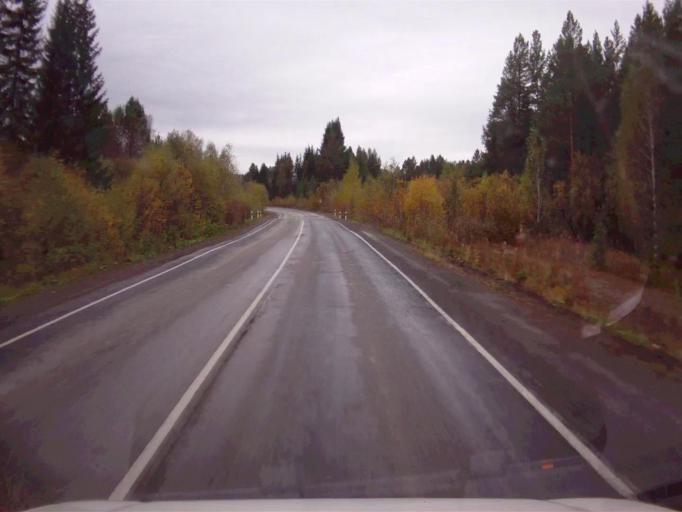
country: RU
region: Chelyabinsk
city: Nyazepetrovsk
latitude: 56.0662
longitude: 59.7002
